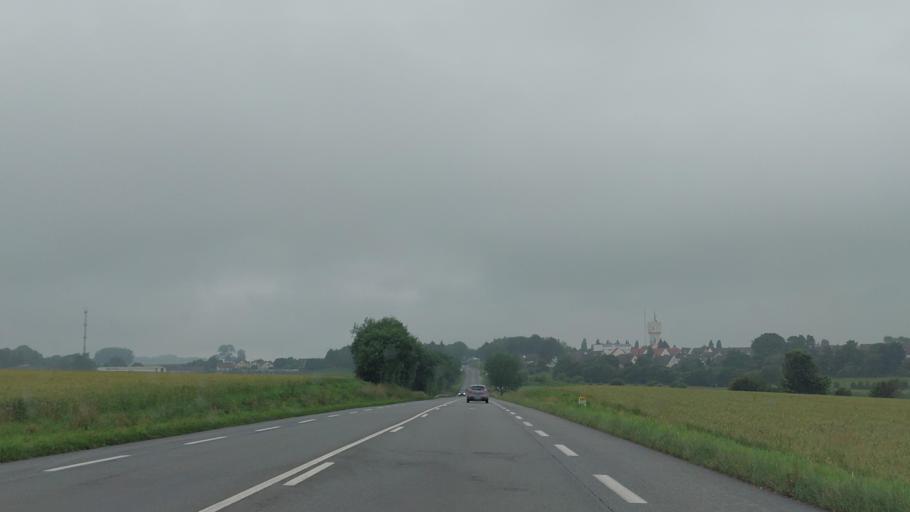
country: FR
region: Picardie
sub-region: Departement de la Somme
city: Friville-Escarbotin
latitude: 50.0732
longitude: 1.5534
